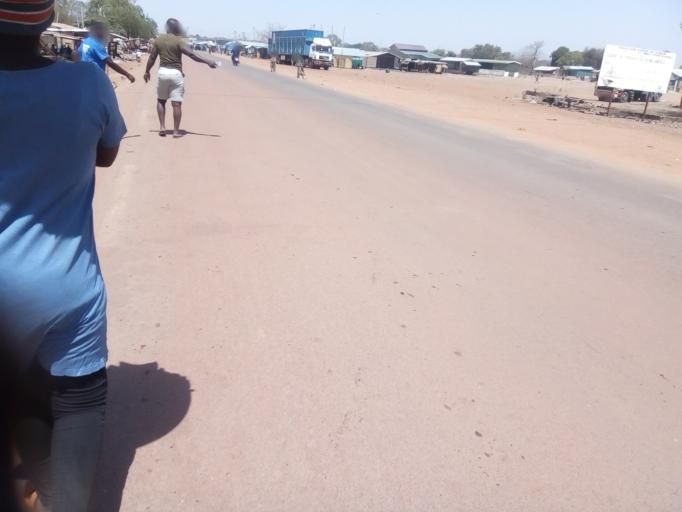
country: GH
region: Upper East
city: Navrongo
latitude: 11.0015
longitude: -1.1157
